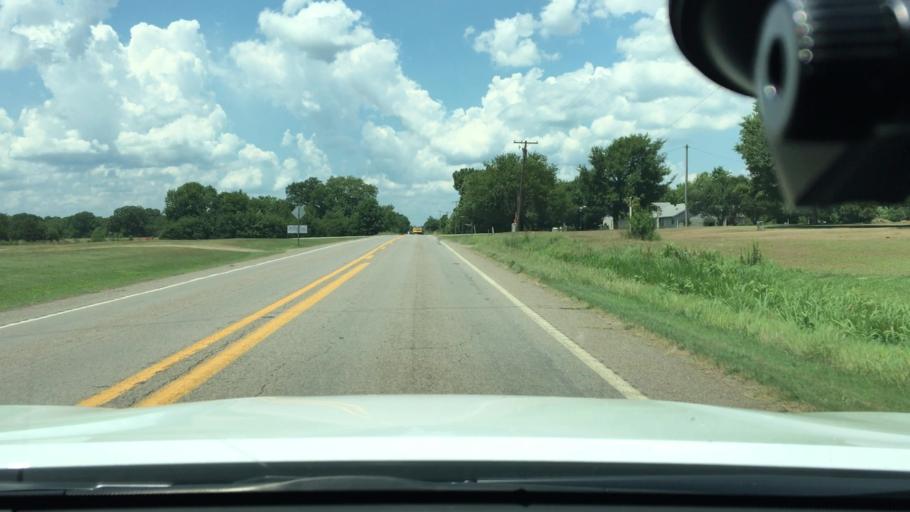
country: US
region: Arkansas
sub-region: Logan County
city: Booneville
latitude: 35.1476
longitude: -93.8519
